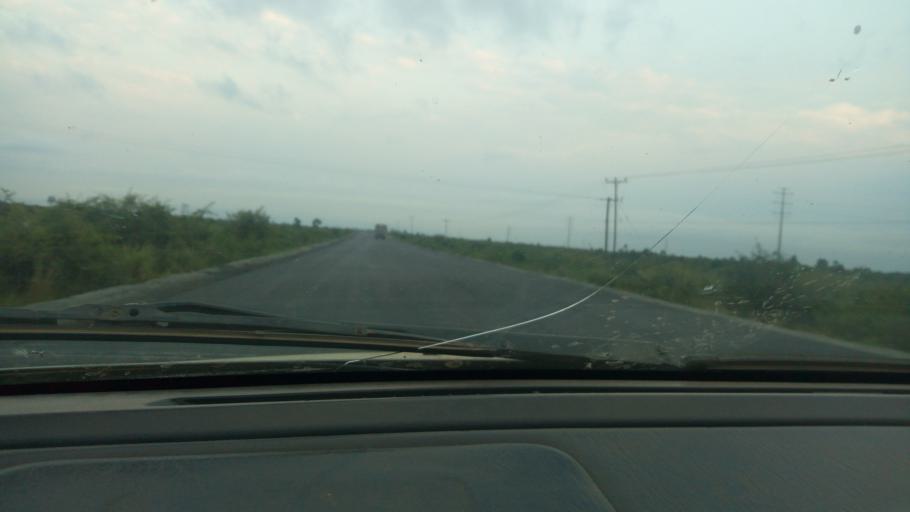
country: UG
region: Western Region
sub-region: Rubirizi District
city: Rubirizi
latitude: -0.1460
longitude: 30.0642
